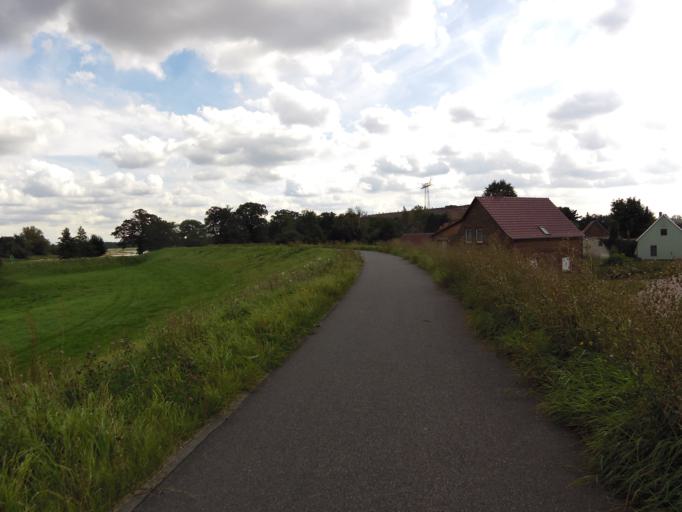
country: DE
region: Saxony-Anhalt
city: Vockerode
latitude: 51.8510
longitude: 12.3537
